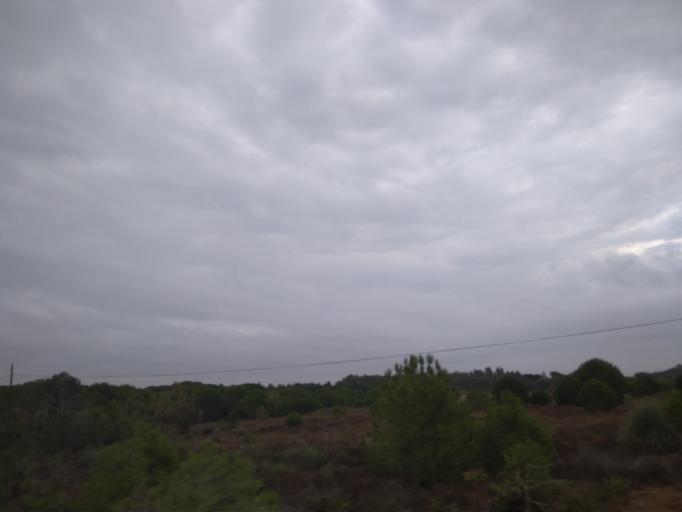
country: PT
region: Faro
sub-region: Faro
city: Faro
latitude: 37.0340
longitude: -7.9845
